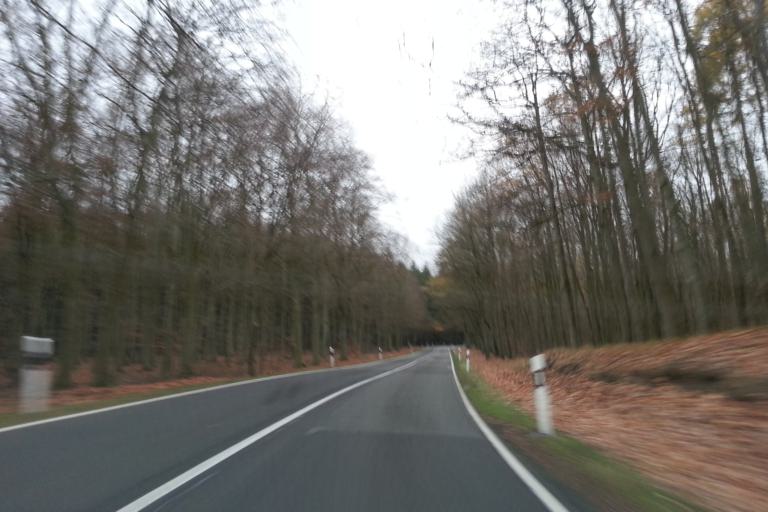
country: DE
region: Mecklenburg-Vorpommern
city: Ferdinandshof
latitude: 53.6030
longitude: 13.8675
